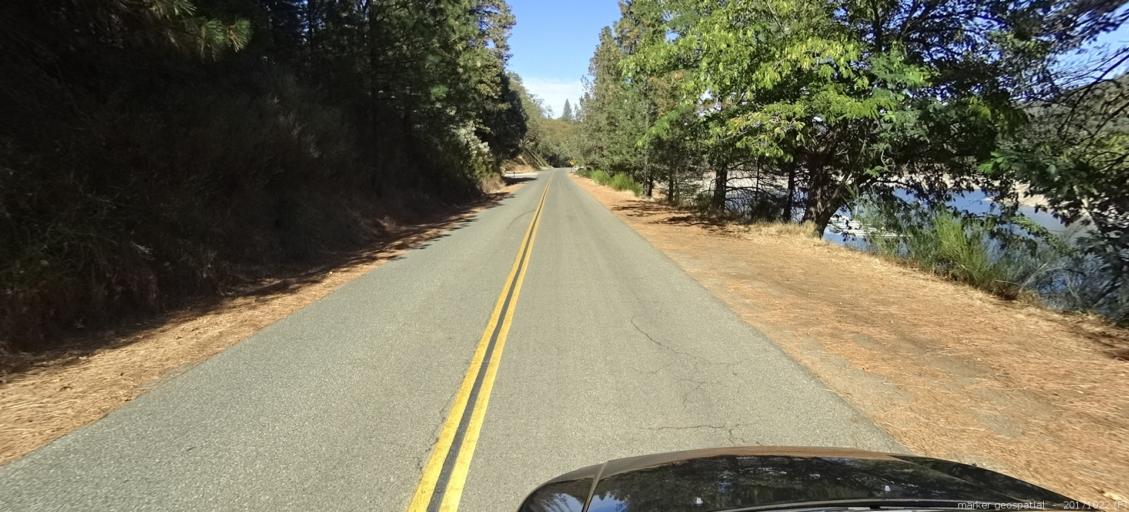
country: US
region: California
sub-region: Shasta County
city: Central Valley (historical)
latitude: 40.8632
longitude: -122.3962
